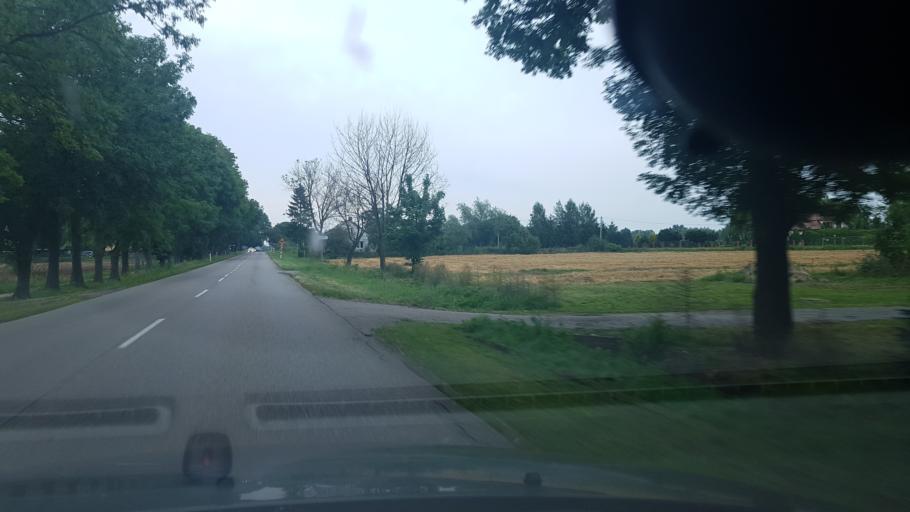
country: PL
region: Pomeranian Voivodeship
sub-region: Powiat nowodworski
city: Nowy Dwor Gdanski
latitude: 54.2257
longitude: 19.1170
